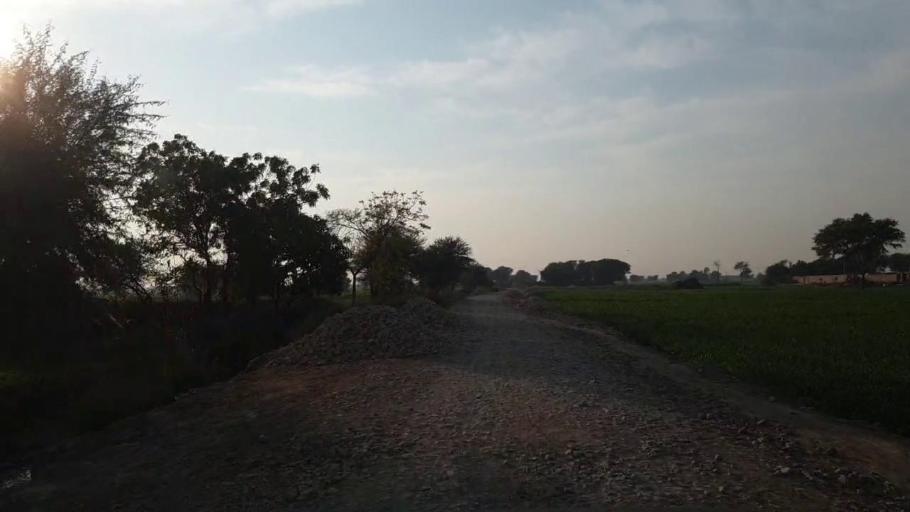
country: PK
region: Sindh
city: Shahpur Chakar
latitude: 26.1523
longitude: 68.6195
